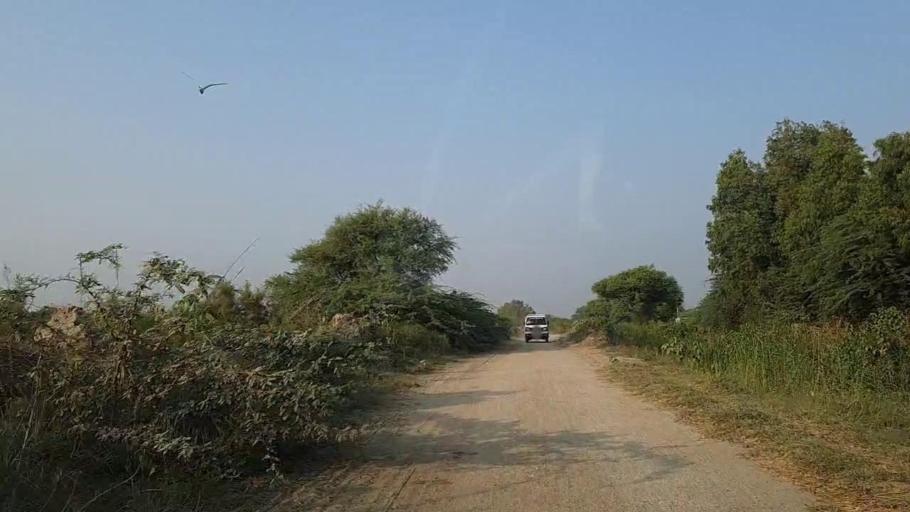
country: PK
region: Sindh
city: Thatta
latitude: 24.6907
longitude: 67.7921
